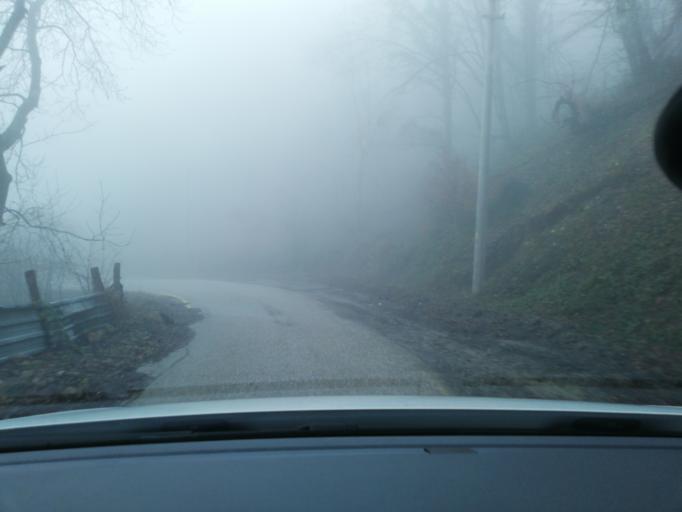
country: TR
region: Duzce
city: Kaynasli
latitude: 40.7530
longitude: 31.3782
